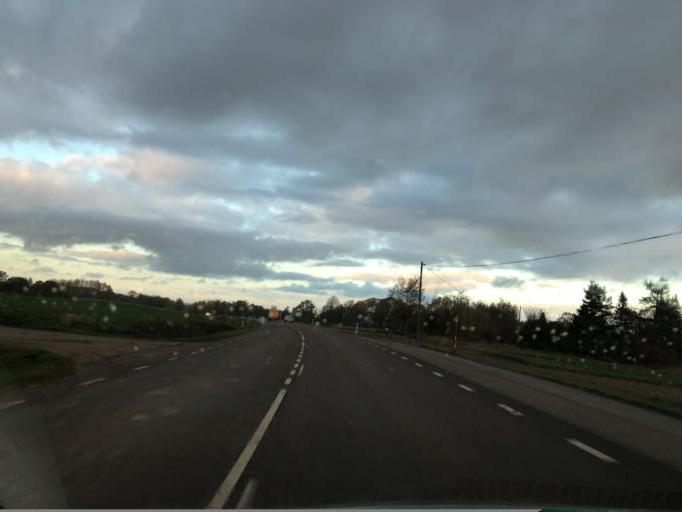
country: SE
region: Skane
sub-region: Klippans Kommun
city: Ljungbyhed
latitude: 55.9877
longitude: 13.2784
